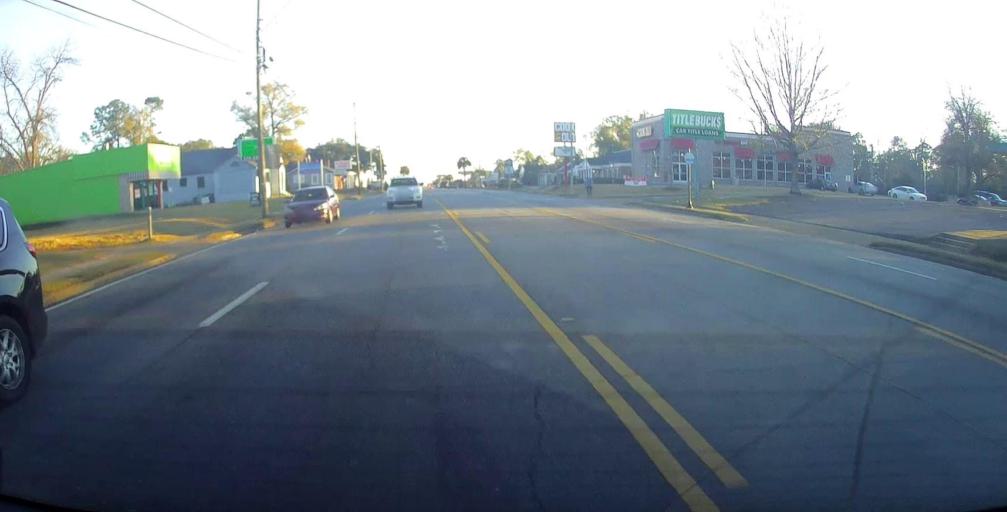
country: US
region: Georgia
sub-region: Dougherty County
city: Albany
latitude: 31.5860
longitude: -84.1762
